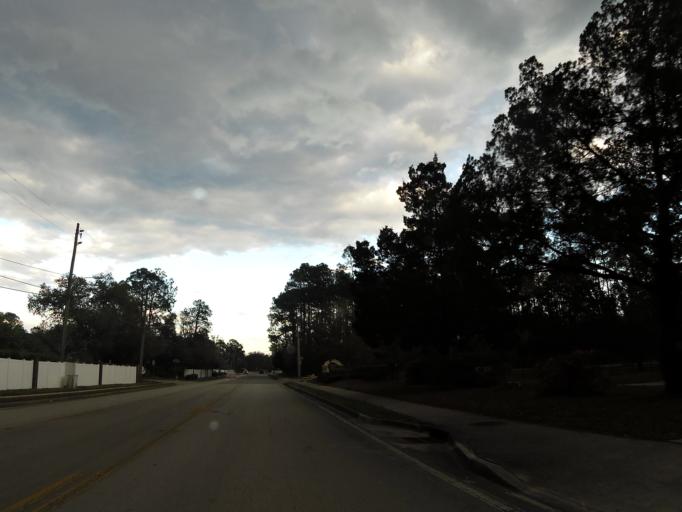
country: US
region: Florida
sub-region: Saint Johns County
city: Fruit Cove
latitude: 30.1724
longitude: -81.5734
